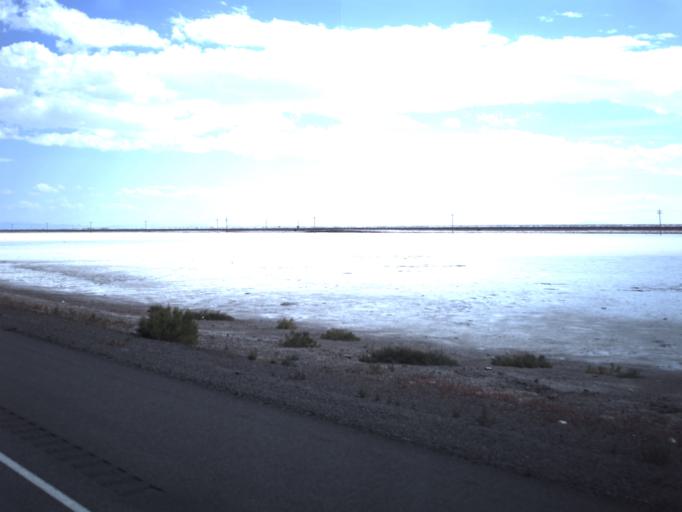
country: US
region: Utah
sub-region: Tooele County
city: Wendover
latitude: 40.7384
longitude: -113.8475
